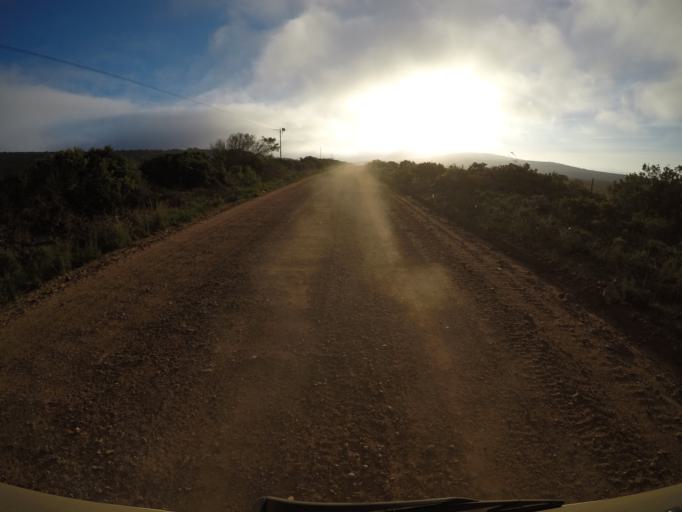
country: ZA
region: Western Cape
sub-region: Eden District Municipality
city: Mossel Bay
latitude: -34.1427
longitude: 22.0315
